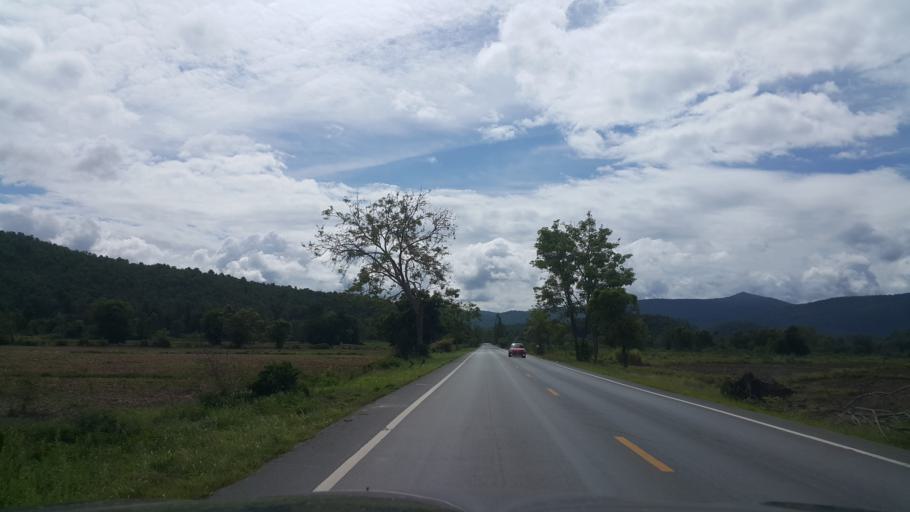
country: TH
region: Uttaradit
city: Thong Saen Khan
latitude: 17.3637
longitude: 100.2375
